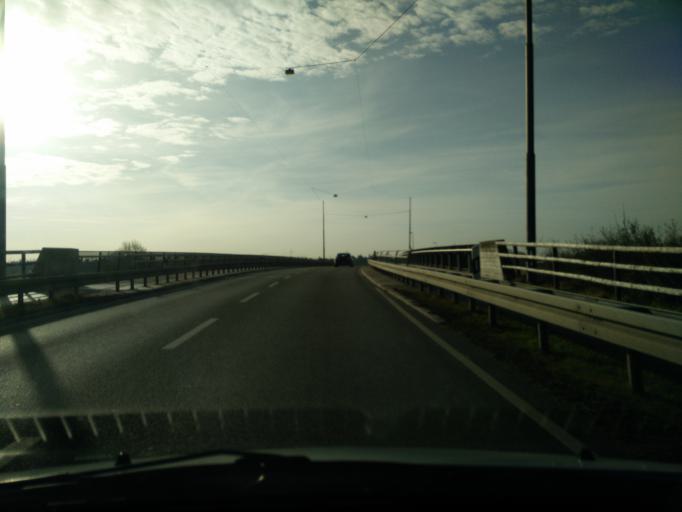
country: DE
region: Bavaria
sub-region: Upper Bavaria
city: Pasing
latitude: 48.1724
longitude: 11.4473
